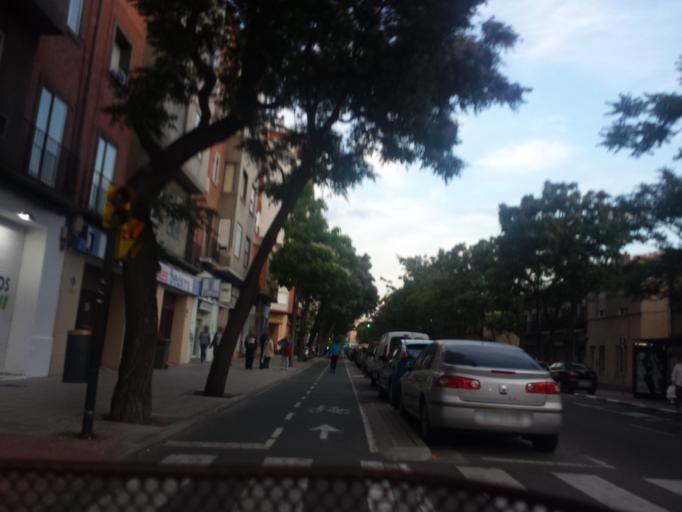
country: ES
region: Aragon
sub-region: Provincia de Zaragoza
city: Delicias
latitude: 41.6482
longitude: -0.9019
